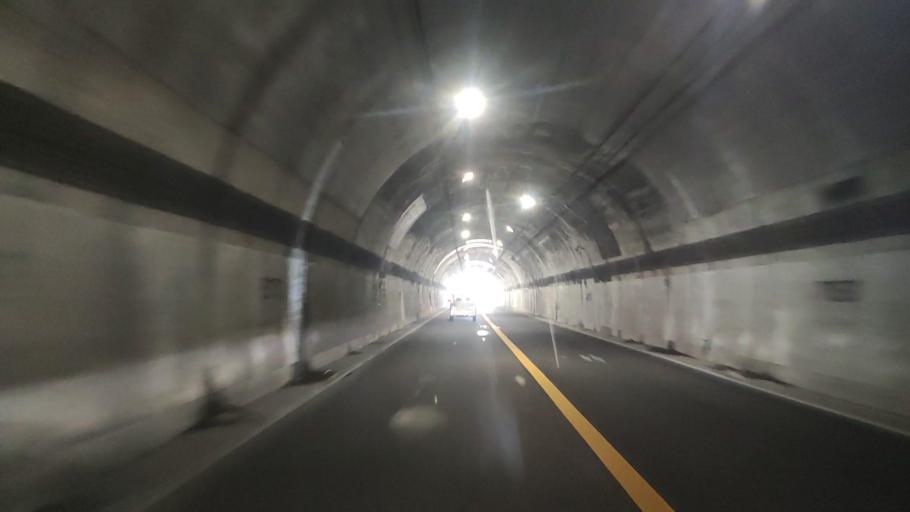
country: JP
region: Wakayama
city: Shingu
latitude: 33.5745
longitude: 135.9172
